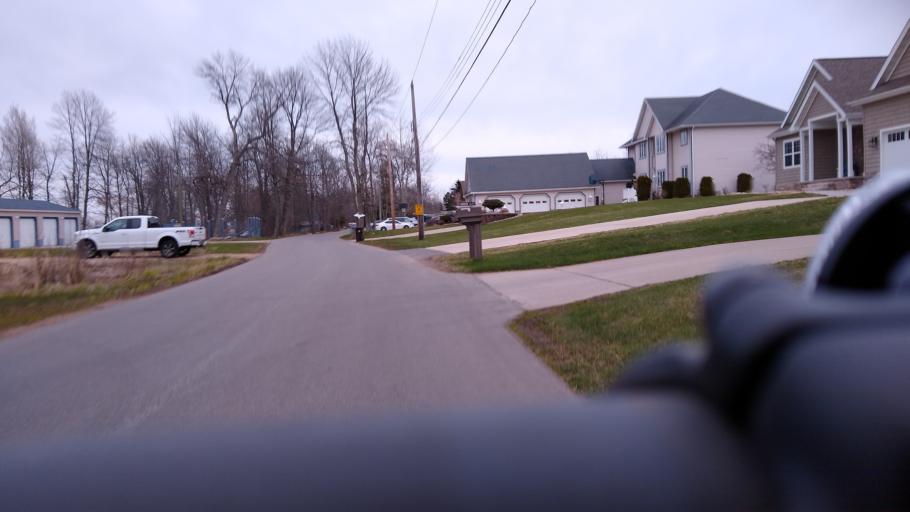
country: US
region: Michigan
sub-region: Delta County
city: Escanaba
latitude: 45.7032
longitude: -87.0897
